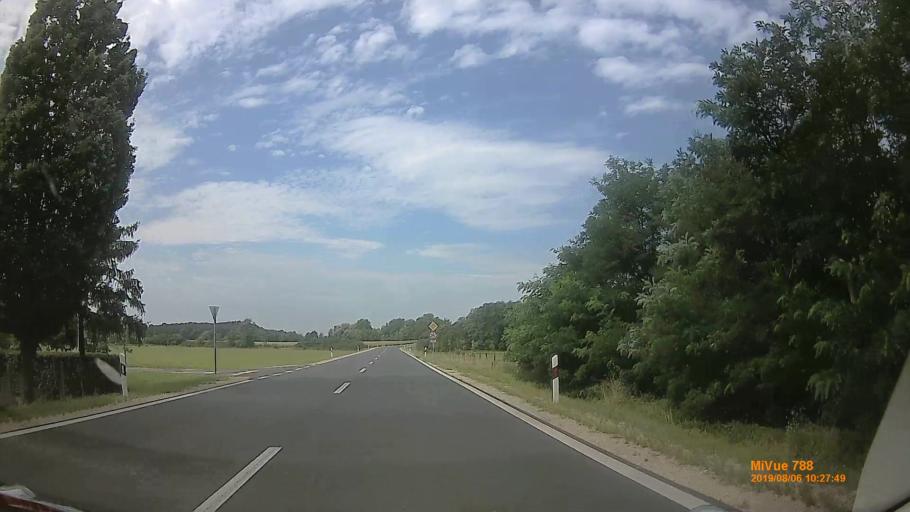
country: HU
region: Vas
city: Kormend
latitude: 47.0405
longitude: 16.6640
